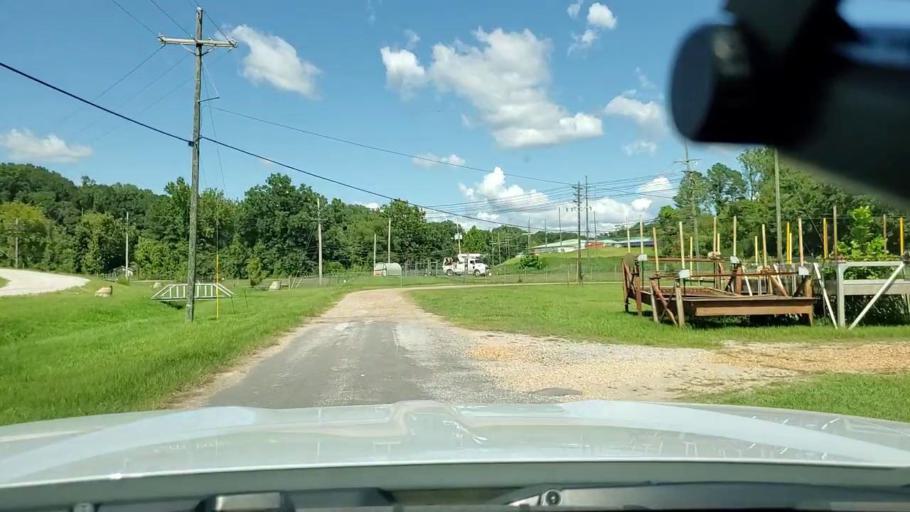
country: US
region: Mississippi
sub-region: Warren County
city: Beechwood
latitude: 32.3085
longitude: -90.8611
